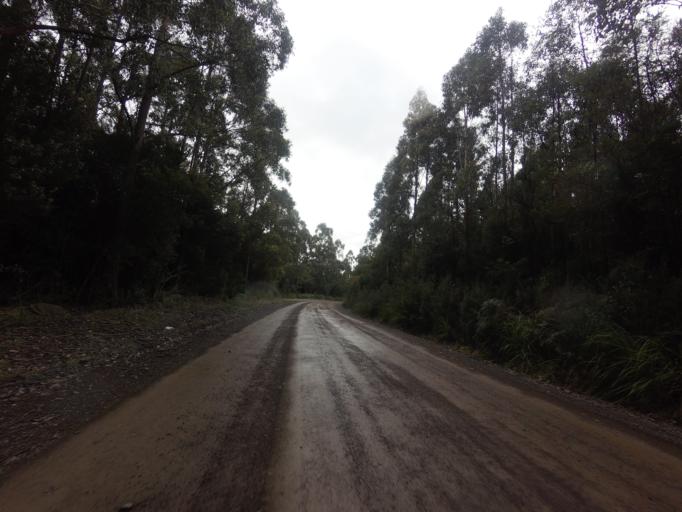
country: AU
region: Tasmania
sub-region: Huon Valley
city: Geeveston
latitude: -43.4685
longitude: 146.8936
